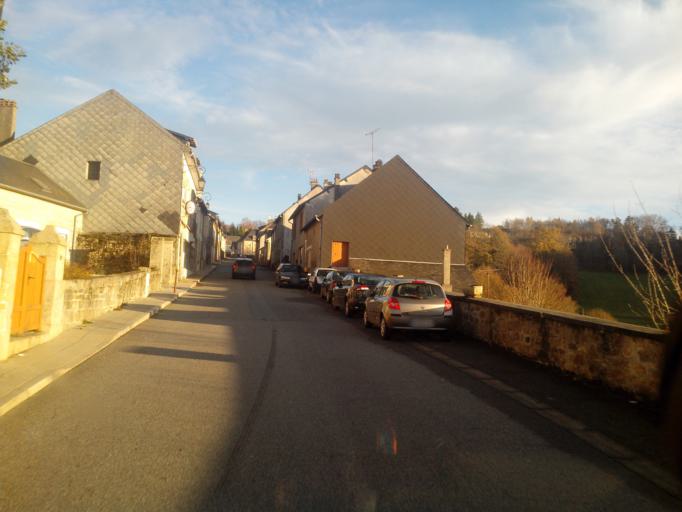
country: FR
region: Limousin
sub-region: Departement de la Correze
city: Bugeat
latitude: 45.5972
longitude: 1.9286
